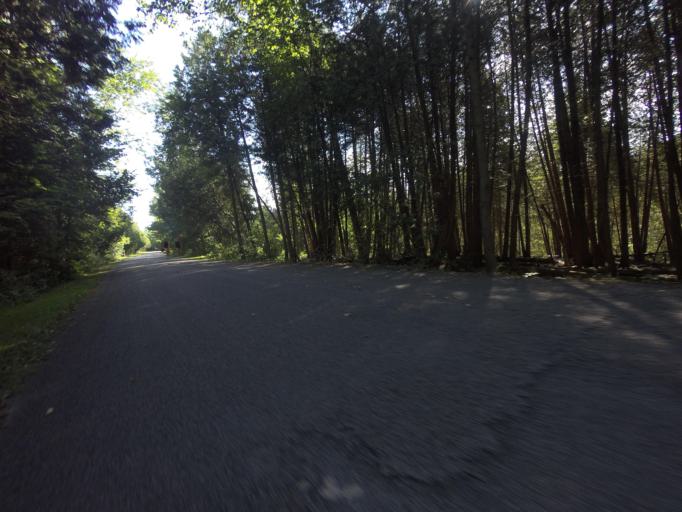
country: CA
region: Ontario
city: Waterloo
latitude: 43.6765
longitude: -80.4472
